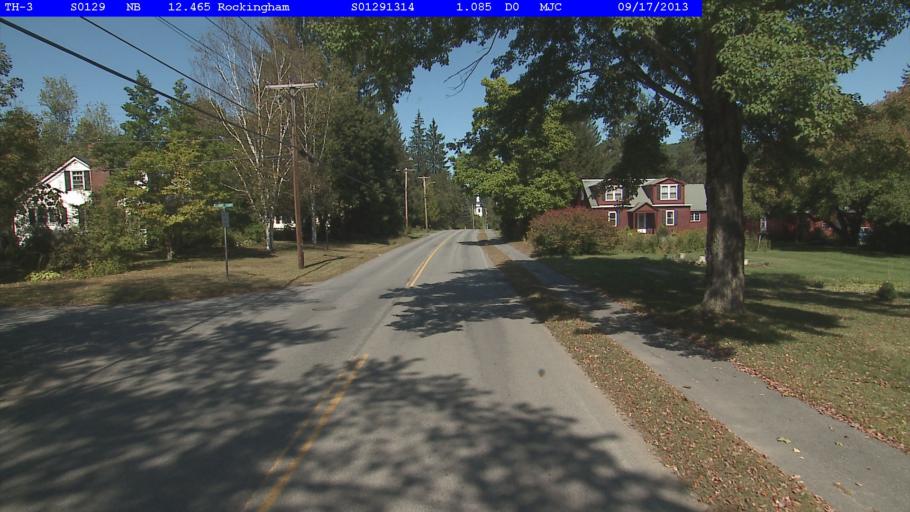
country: US
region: Vermont
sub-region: Windham County
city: Rockingham
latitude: 43.1352
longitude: -72.5109
